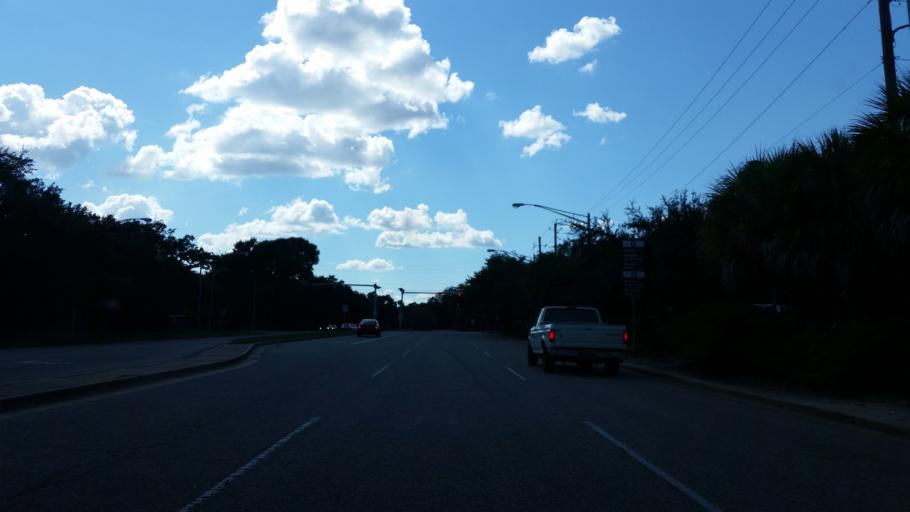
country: US
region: Alabama
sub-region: Mobile County
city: Mobile
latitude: 30.6839
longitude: -88.0477
